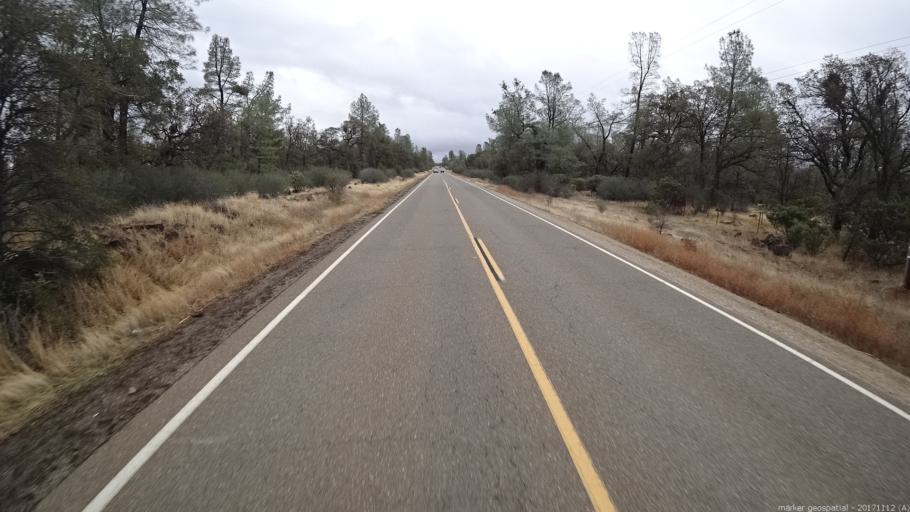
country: US
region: California
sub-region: Shasta County
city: Shingletown
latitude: 40.4922
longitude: -122.0528
